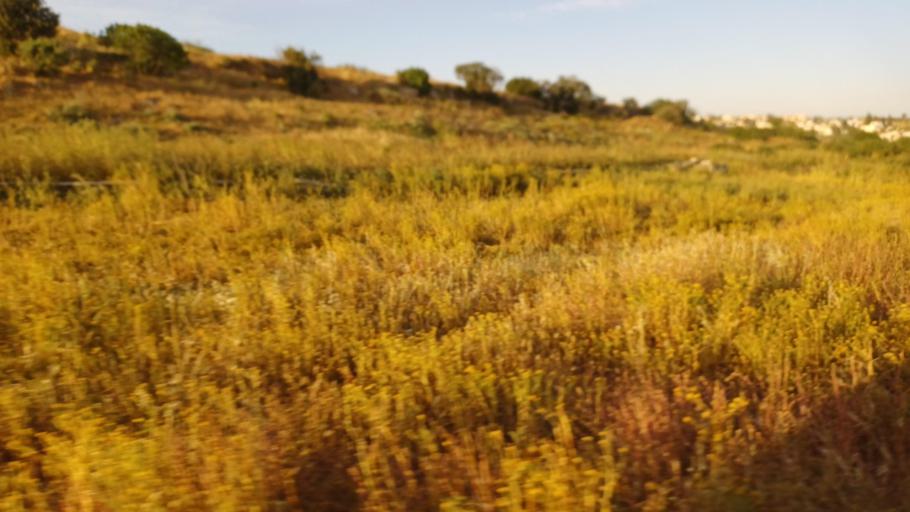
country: CY
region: Lefkosia
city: Kokkinotrimithia
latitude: 35.1713
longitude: 33.1569
